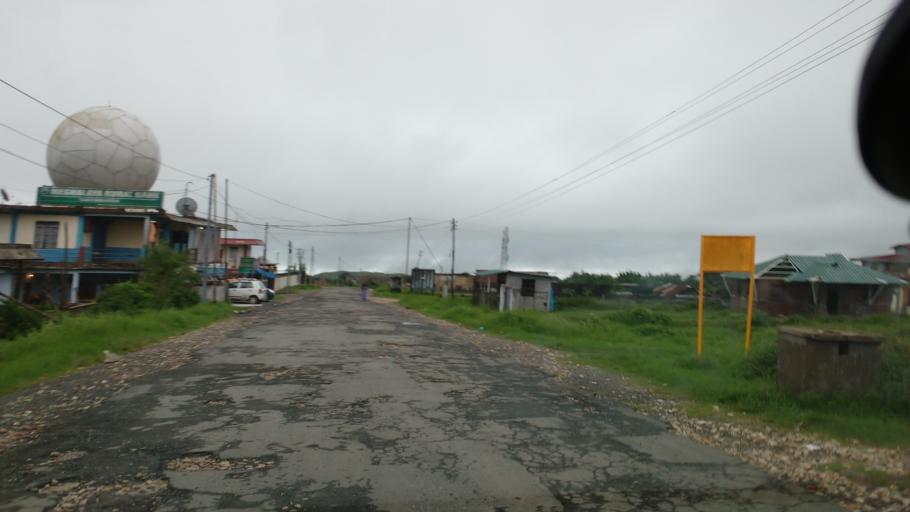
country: IN
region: Meghalaya
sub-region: East Khasi Hills
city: Cherrapunji
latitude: 25.2696
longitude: 91.7326
